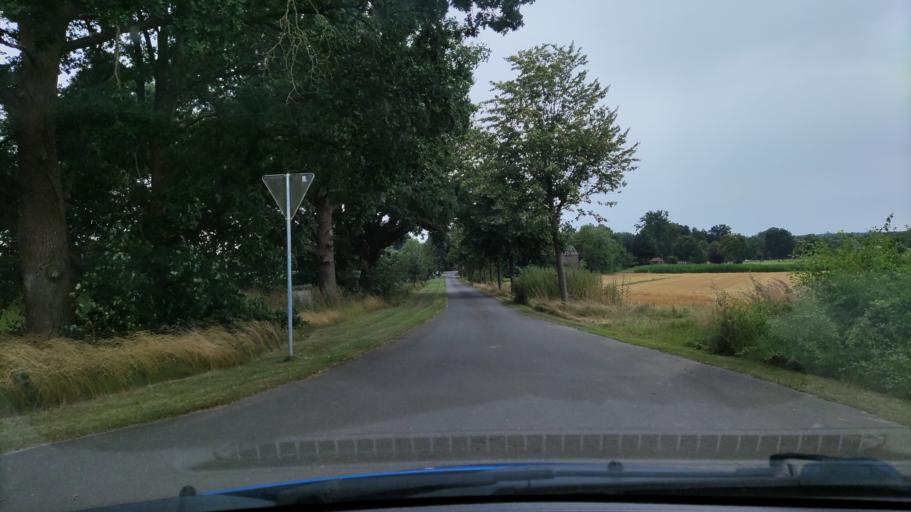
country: DE
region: Lower Saxony
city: Rosche
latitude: 53.0041
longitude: 10.7660
